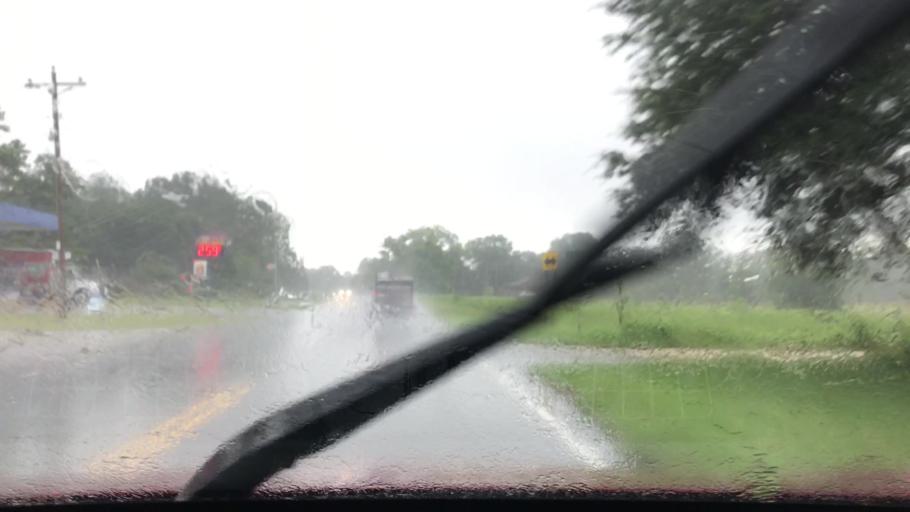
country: US
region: South Carolina
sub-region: Horry County
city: Red Hill
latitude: 33.9021
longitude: -78.8944
